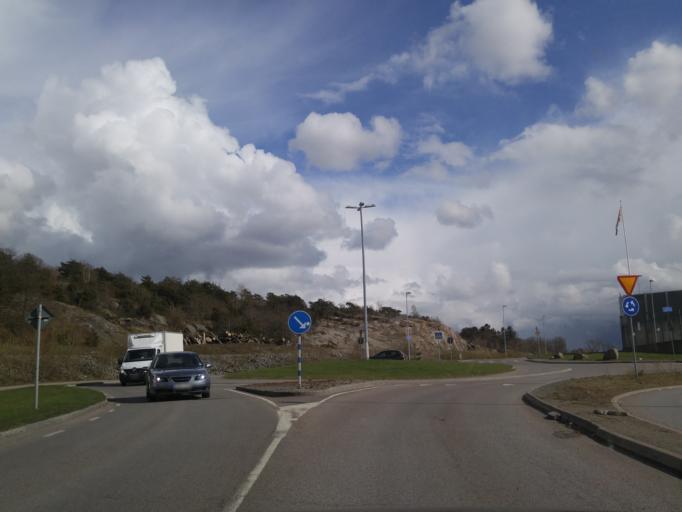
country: SE
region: Vaestra Goetaland
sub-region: Goteborg
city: Majorna
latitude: 57.6579
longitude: 11.9477
